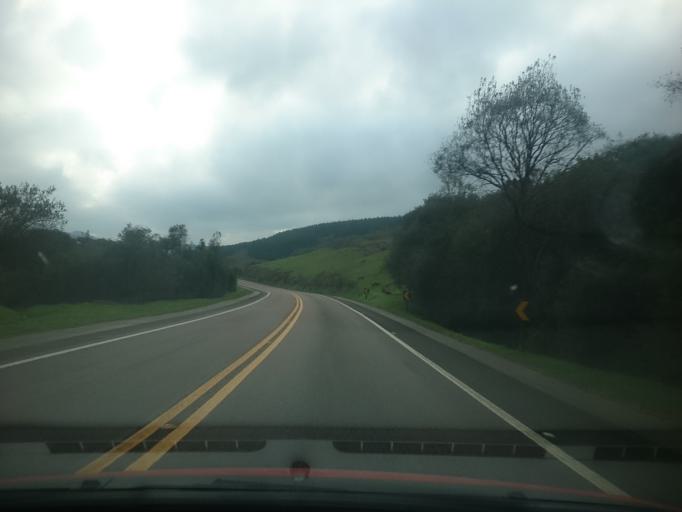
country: BR
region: Santa Catarina
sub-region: Lages
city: Lages
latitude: -27.8814
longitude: -50.4100
